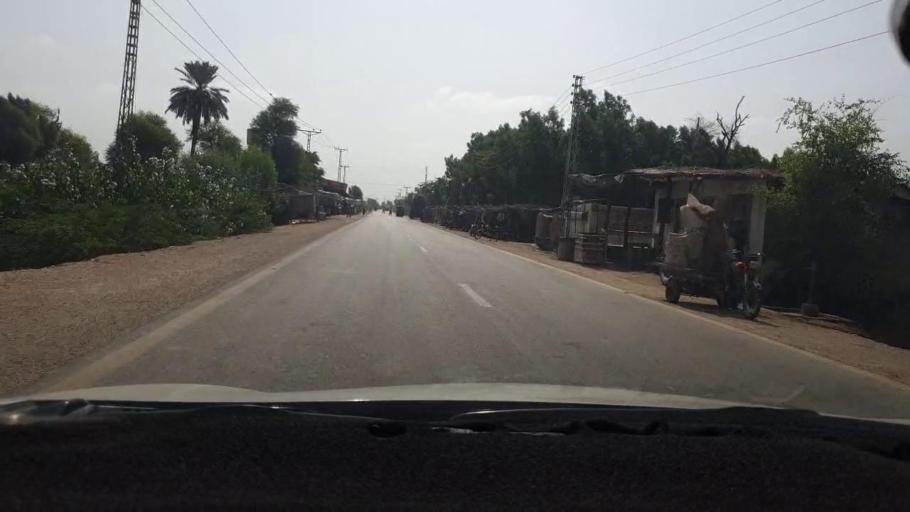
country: PK
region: Sindh
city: Mirpur Khas
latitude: 25.7218
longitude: 69.1155
